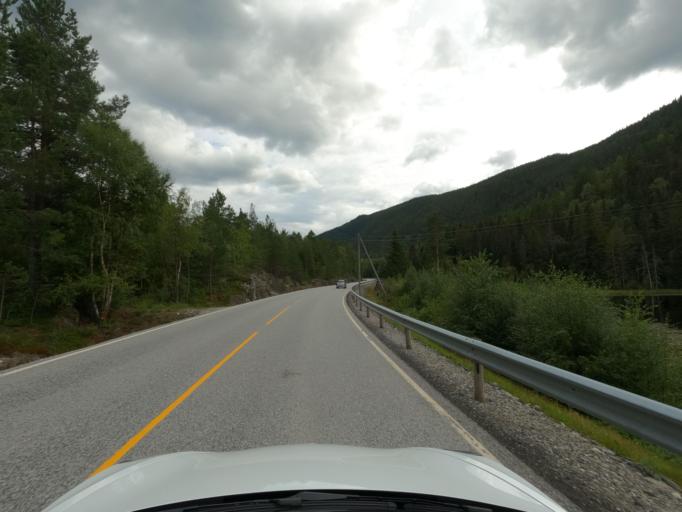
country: NO
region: Telemark
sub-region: Hjartdal
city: Sauland
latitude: 59.8602
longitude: 8.9399
